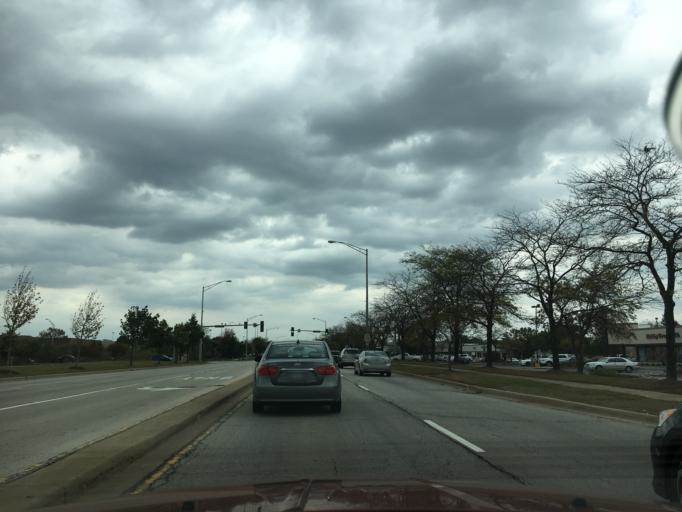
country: US
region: Illinois
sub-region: Cook County
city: Orland Hills
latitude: 41.6075
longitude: -87.8481
